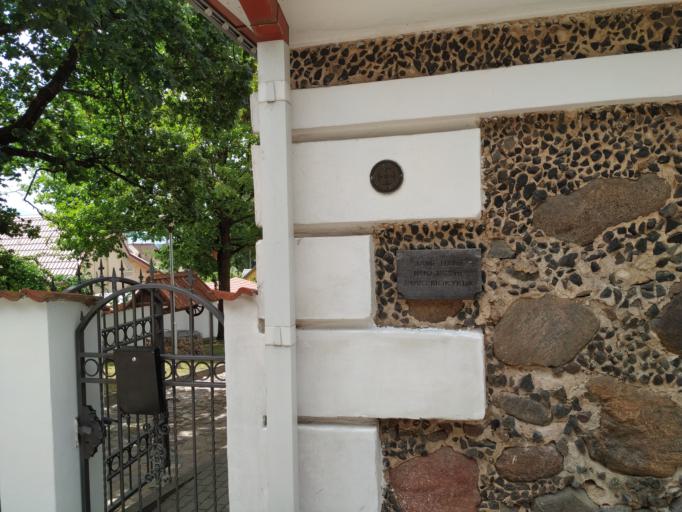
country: LT
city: Kupiskis
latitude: 55.8422
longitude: 24.9755
